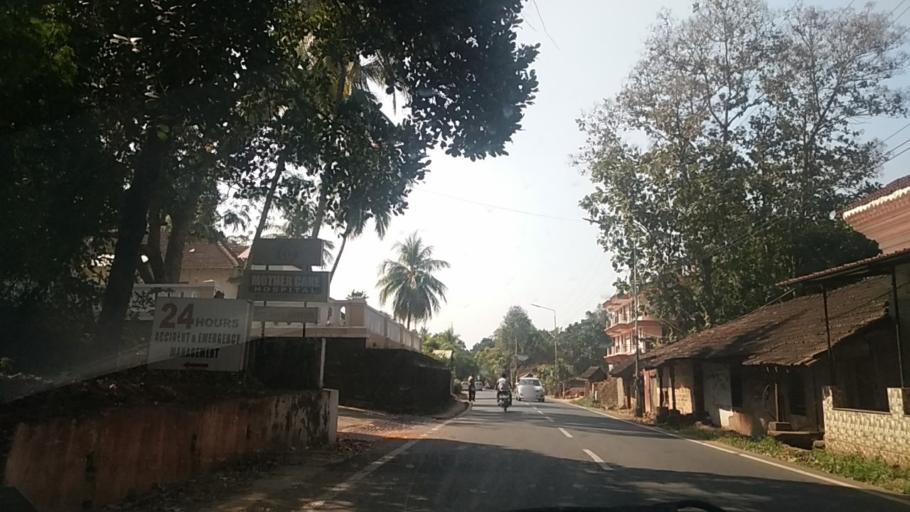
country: IN
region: Goa
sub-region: South Goa
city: Madgaon
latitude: 15.2827
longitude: 73.9640
